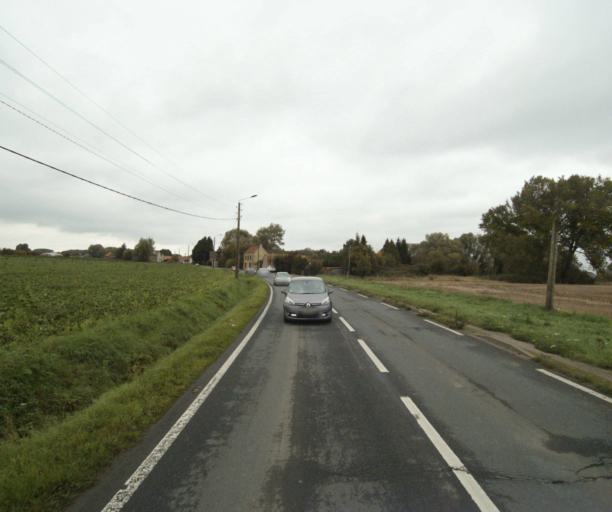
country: FR
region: Nord-Pas-de-Calais
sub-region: Departement du Nord
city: Wavrin
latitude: 50.5841
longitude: 2.9315
